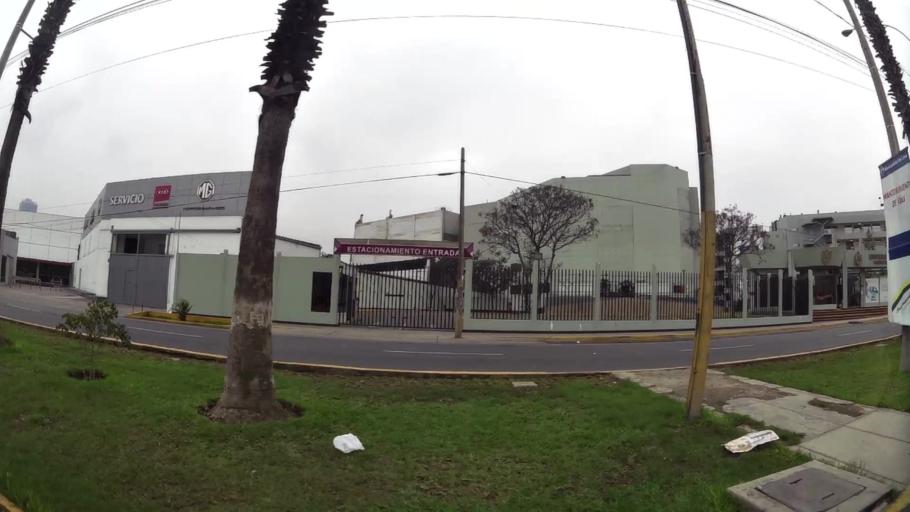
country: PE
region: Lima
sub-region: Lima
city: San Isidro
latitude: -12.1050
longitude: -77.0181
